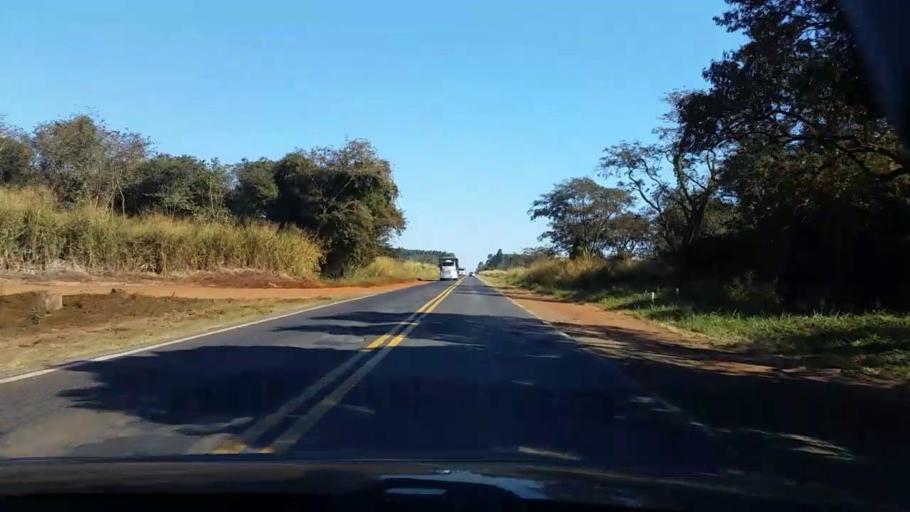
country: BR
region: Sao Paulo
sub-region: Avare
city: Avare
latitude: -22.9152
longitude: -48.7783
